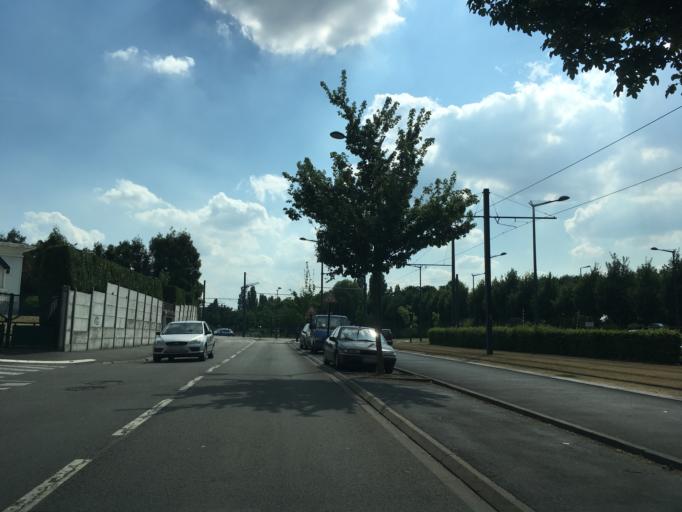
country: FR
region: Nord-Pas-de-Calais
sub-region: Departement du Nord
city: Valenciennes
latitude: 50.3478
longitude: 3.5189
